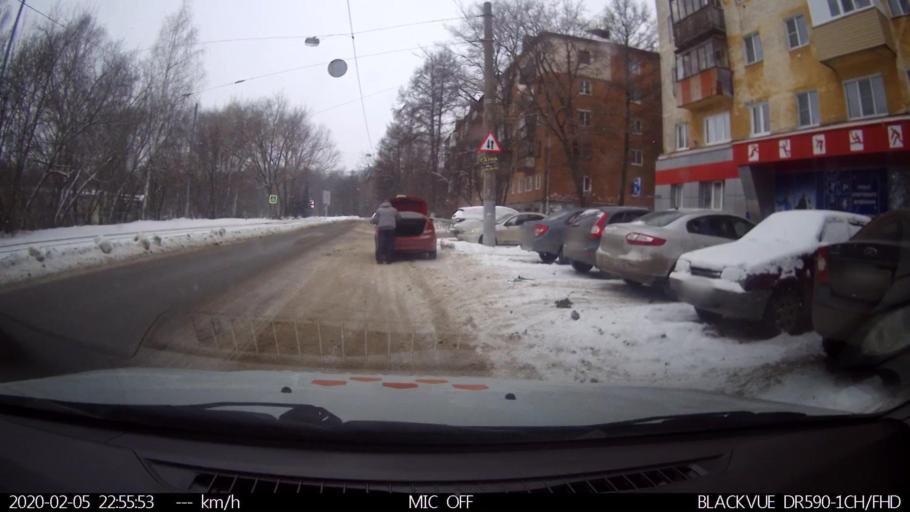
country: RU
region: Penza
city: Bogoslovka
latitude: 53.3121
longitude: 44.8189
